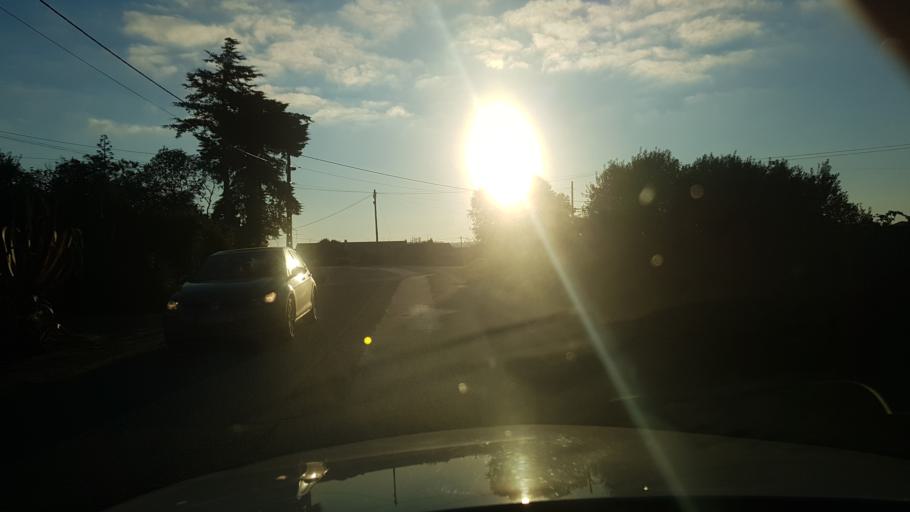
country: PT
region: Santarem
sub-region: Torres Novas
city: Torres Novas
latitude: 39.5546
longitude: -8.5676
